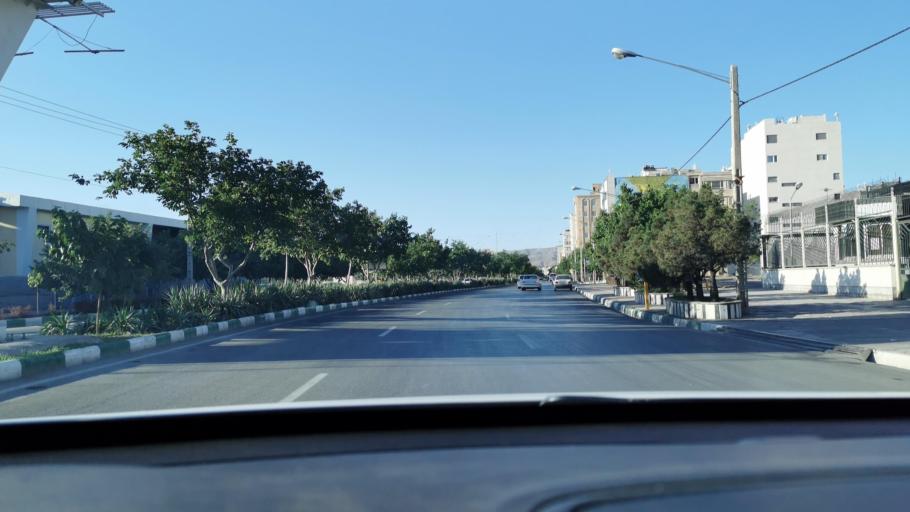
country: IR
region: Razavi Khorasan
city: Mashhad
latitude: 36.3554
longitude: 59.4880
